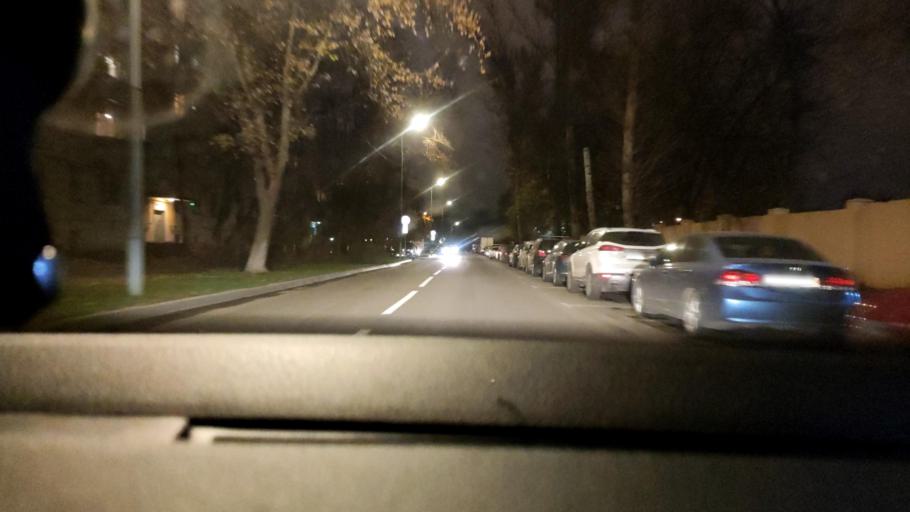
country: RU
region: Moscow
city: Lyublino
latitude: 55.6839
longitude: 37.7566
